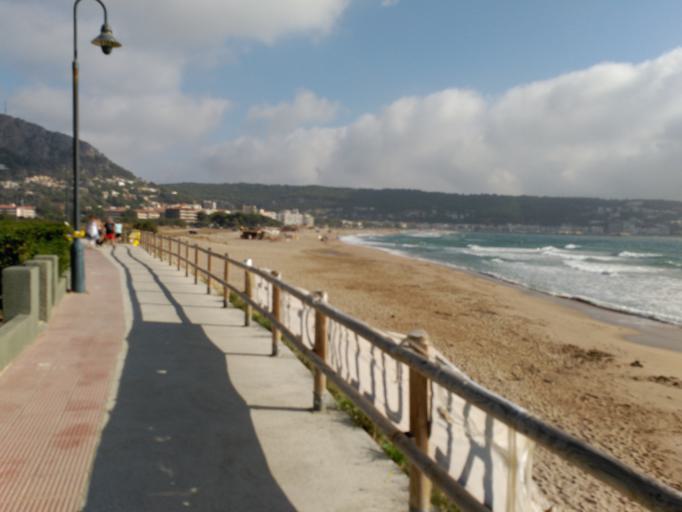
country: ES
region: Catalonia
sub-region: Provincia de Girona
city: Torroella de Montgri
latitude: 42.0430
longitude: 3.1963
